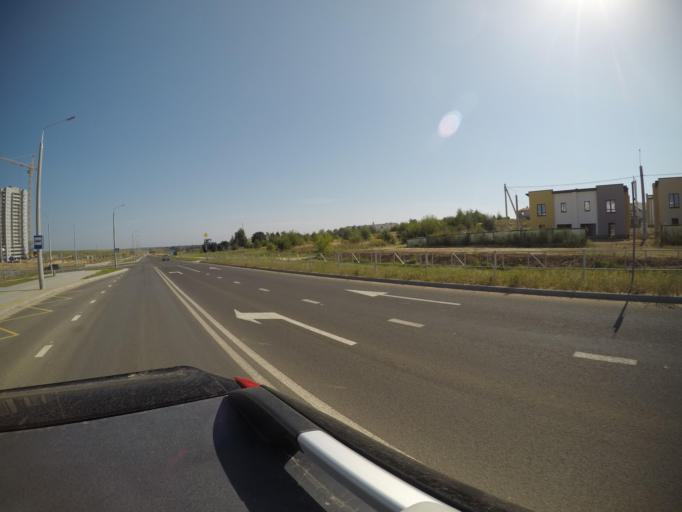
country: BY
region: Grodnenskaya
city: Hrodna
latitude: 53.7181
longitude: 23.8820
